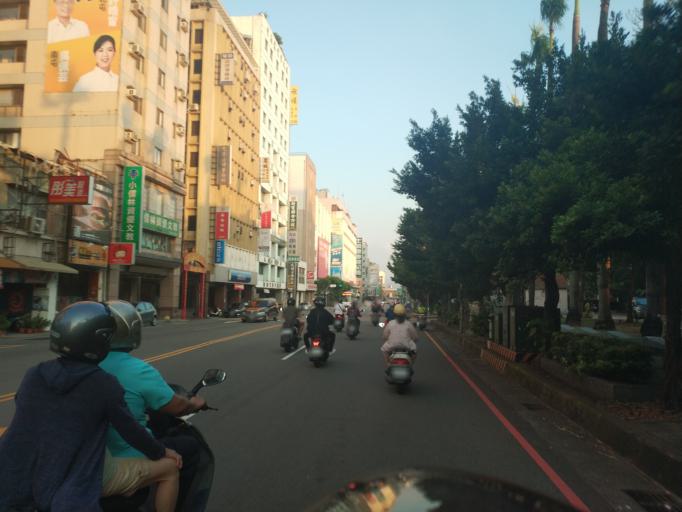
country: TW
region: Taiwan
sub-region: Taichung City
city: Taichung
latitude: 24.1400
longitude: 120.6775
